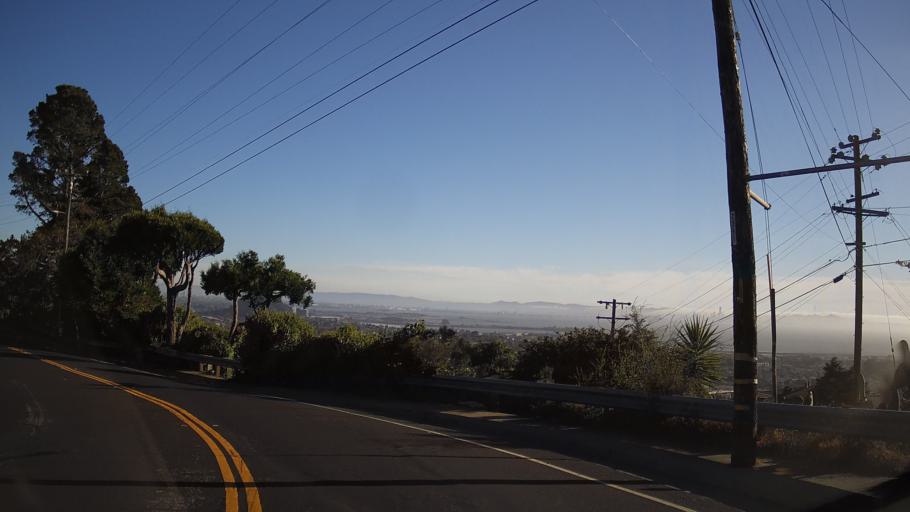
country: US
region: California
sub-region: Contra Costa County
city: East Richmond Heights
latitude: 37.9316
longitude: -122.3102
